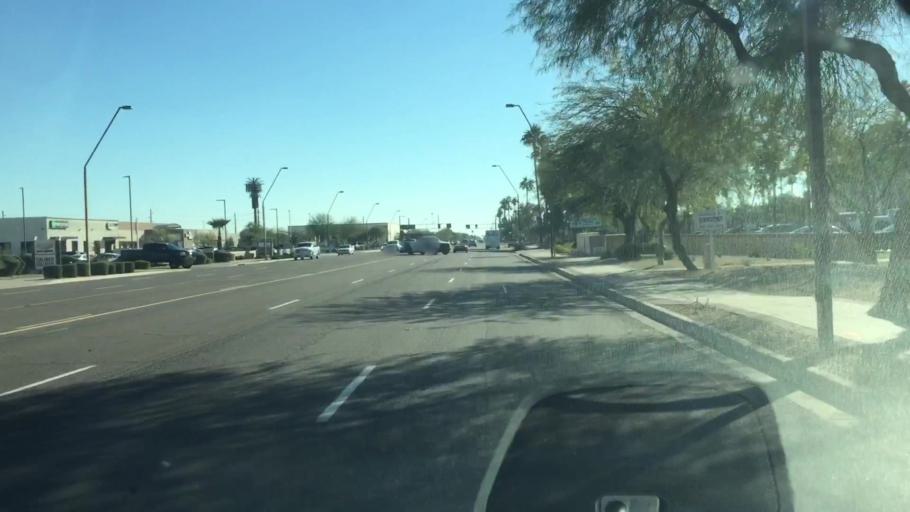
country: US
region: Arizona
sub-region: Maricopa County
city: Guadalupe
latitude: 33.3426
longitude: -111.9632
